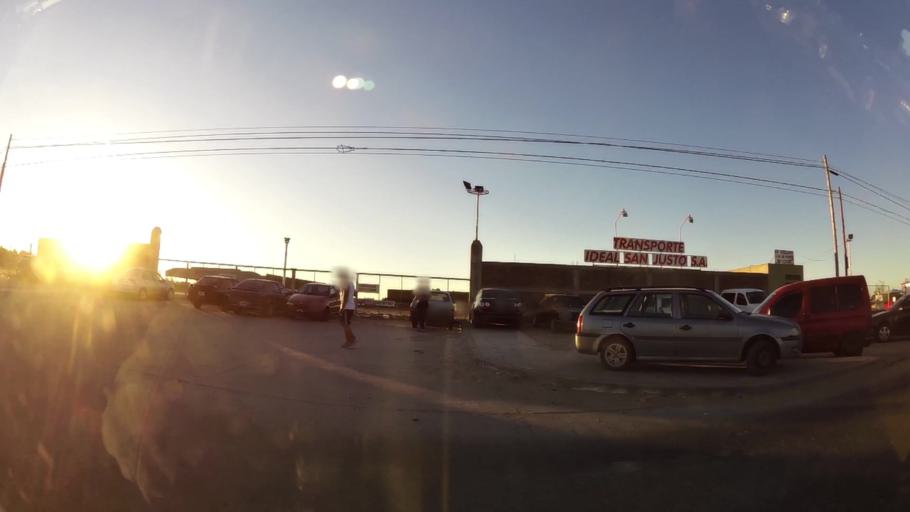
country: AR
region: Buenos Aires
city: Pontevedra
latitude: -34.7452
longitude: -58.6093
